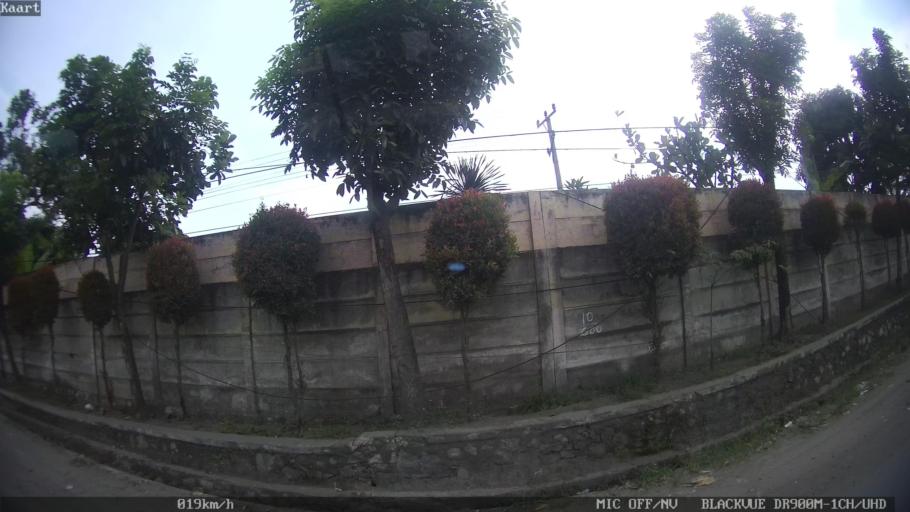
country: ID
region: Lampung
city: Bandarlampung
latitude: -5.4065
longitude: 105.2928
